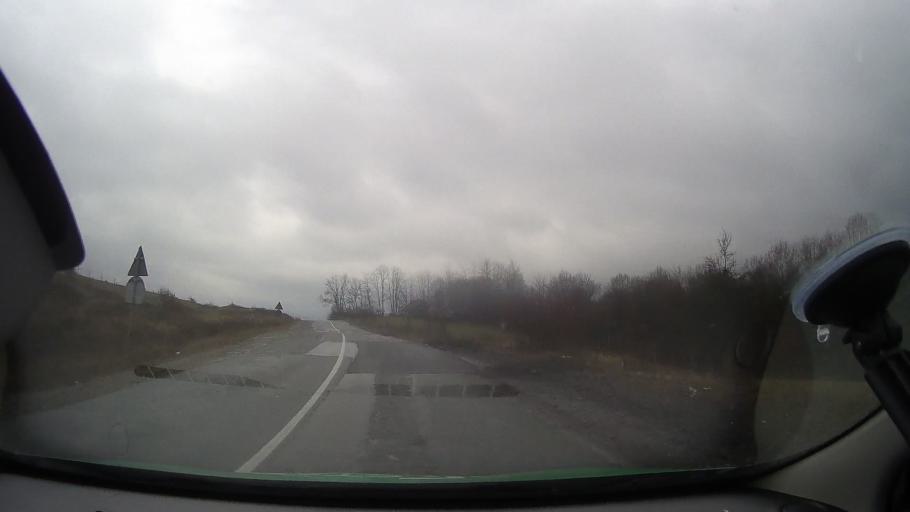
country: RO
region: Arad
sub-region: Comuna Varfurile
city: Varfurile
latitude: 46.2978
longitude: 22.5388
